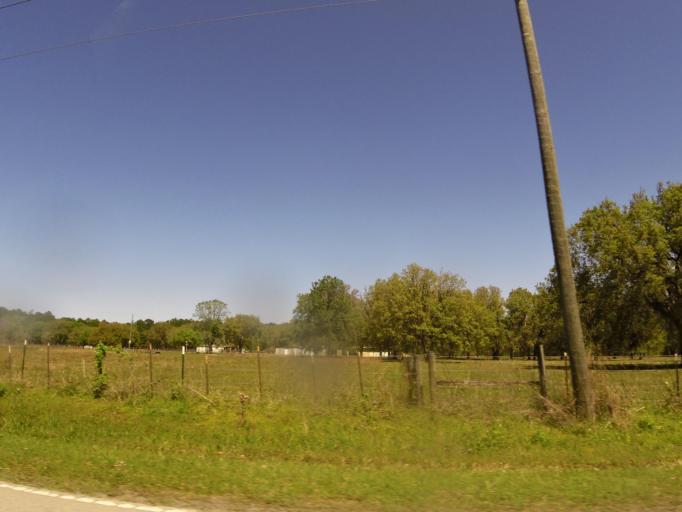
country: US
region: Florida
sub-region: Putnam County
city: East Palatka
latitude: 29.7747
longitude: -81.6060
